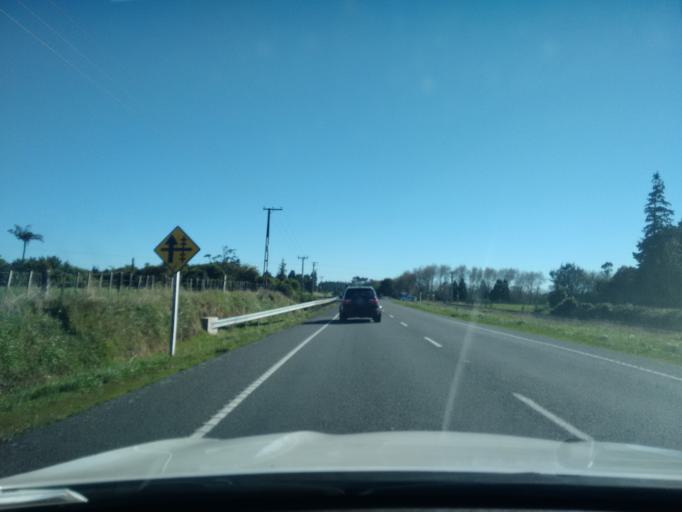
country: NZ
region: Taranaki
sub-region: New Plymouth District
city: New Plymouth
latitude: -39.1844
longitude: 174.2211
